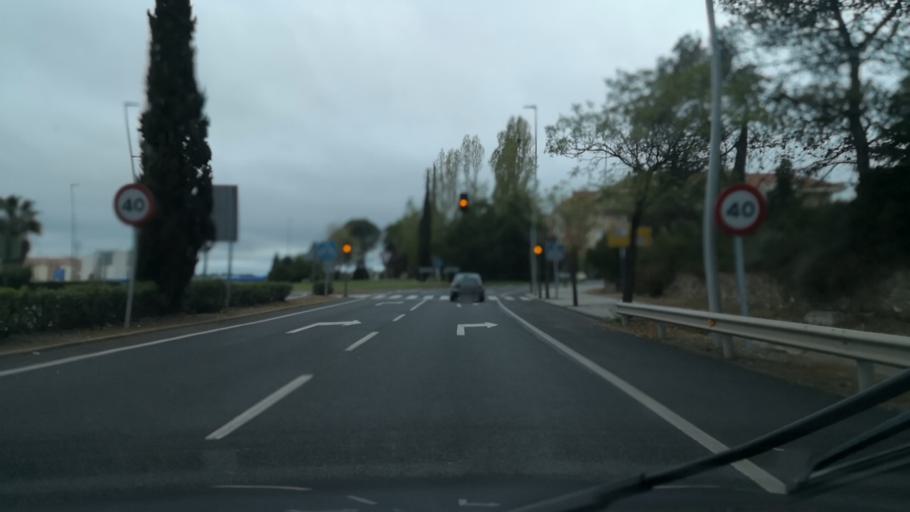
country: ES
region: Extremadura
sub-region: Provincia de Caceres
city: Caceres
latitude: 39.4692
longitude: -6.3949
